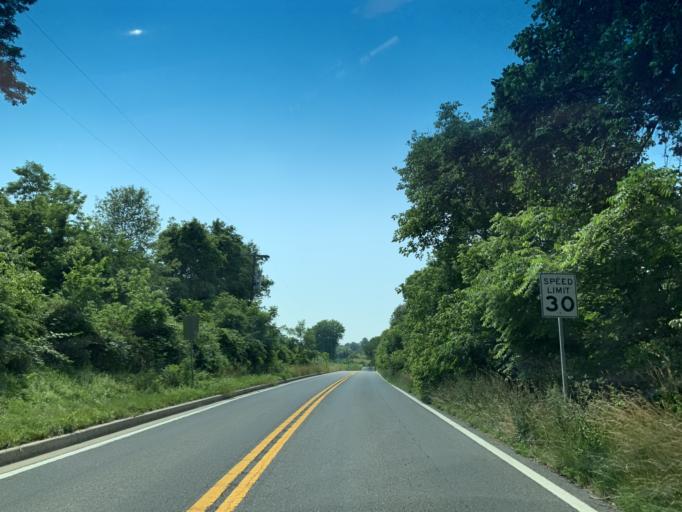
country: US
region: Maryland
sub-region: Frederick County
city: Green Valley
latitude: 39.2774
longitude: -77.3267
